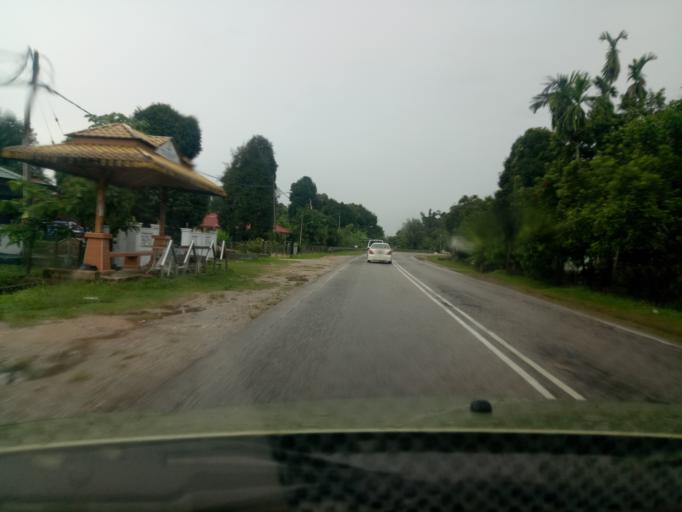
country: MY
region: Penang
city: Tasek Glugor
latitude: 5.5255
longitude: 100.5740
